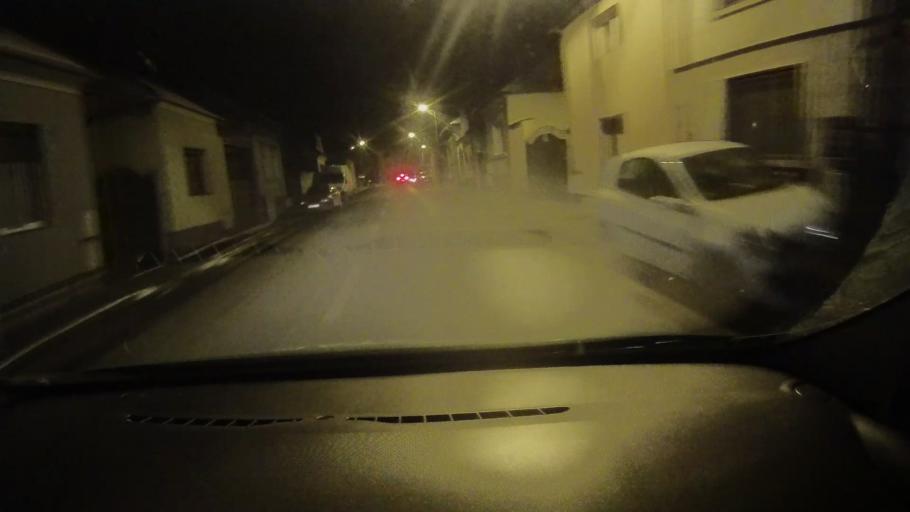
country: RO
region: Brasov
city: Brasov
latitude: 45.6606
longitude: 25.5871
